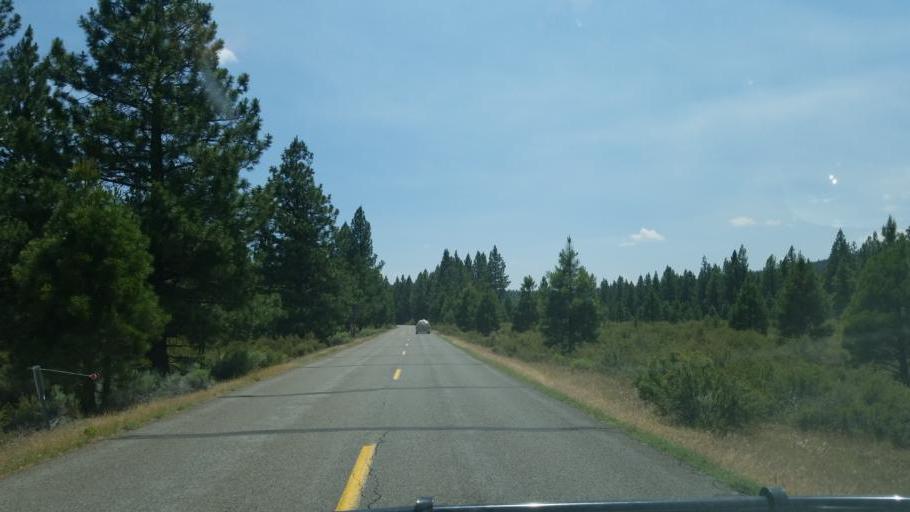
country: US
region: California
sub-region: Lassen County
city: Susanville
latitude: 40.5745
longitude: -120.8440
